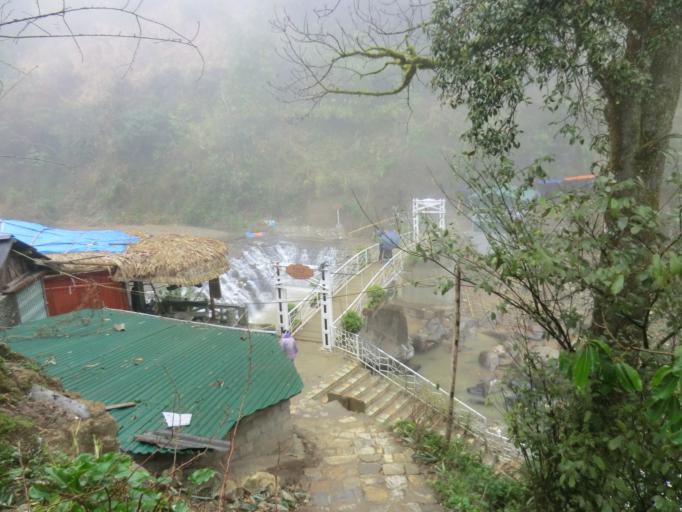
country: VN
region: Lao Cai
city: Sa Pa
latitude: 22.3274
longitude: 103.8340
